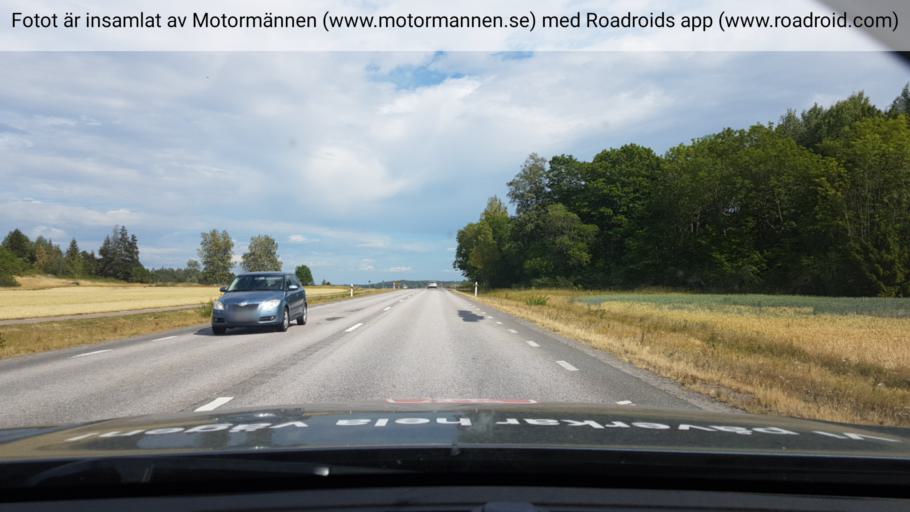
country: SE
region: Uppsala
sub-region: Uppsala Kommun
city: Uppsala
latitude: 59.8518
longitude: 17.4501
